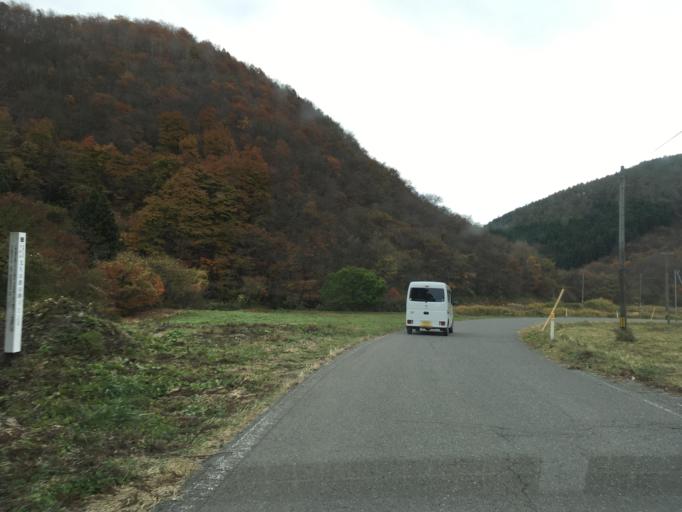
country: JP
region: Iwate
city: Mizusawa
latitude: 39.1064
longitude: 141.3291
